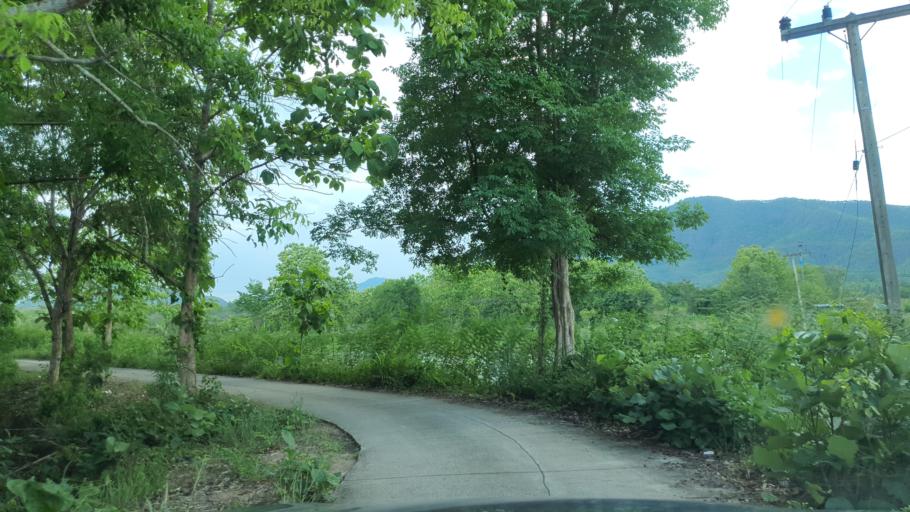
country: TH
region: Chiang Mai
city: Mae Taeng
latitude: 19.1186
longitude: 99.0621
